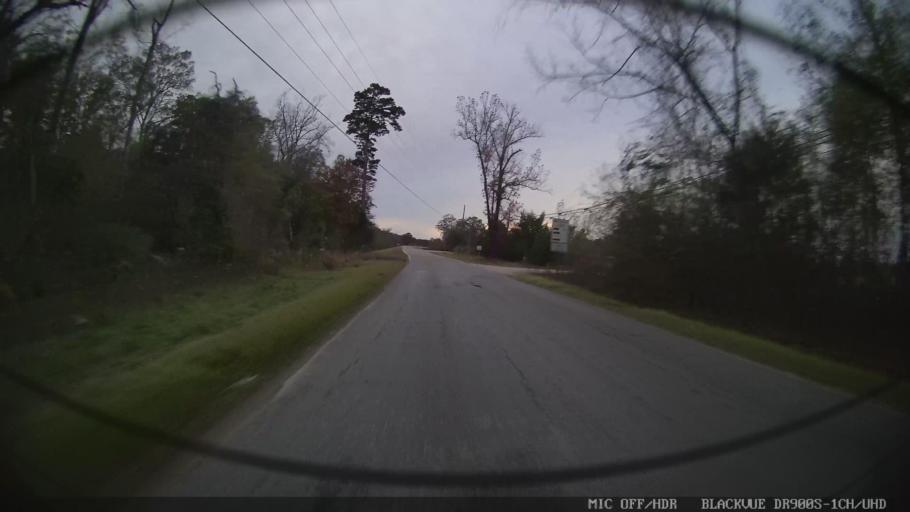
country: US
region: Mississippi
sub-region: Clarke County
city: Quitman
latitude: 32.0420
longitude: -88.7374
